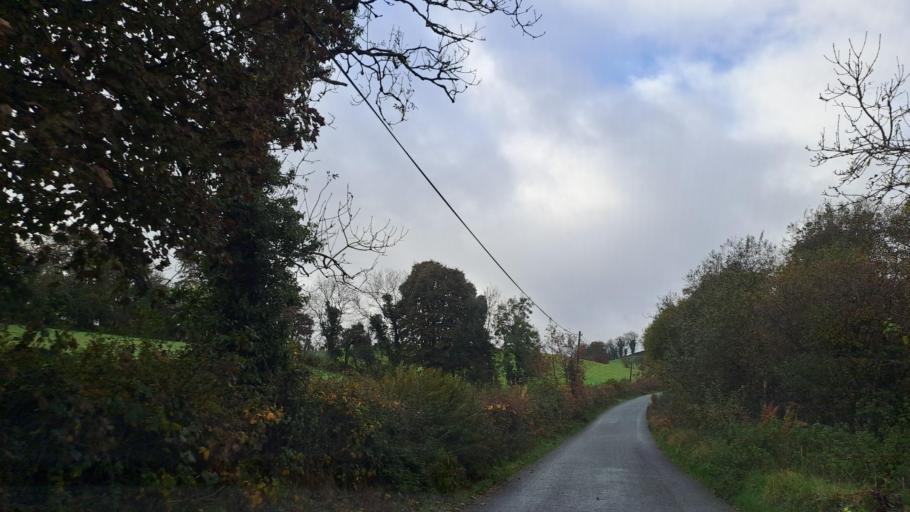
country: IE
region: Ulster
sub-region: An Cabhan
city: Bailieborough
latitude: 53.9600
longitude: -6.9864
